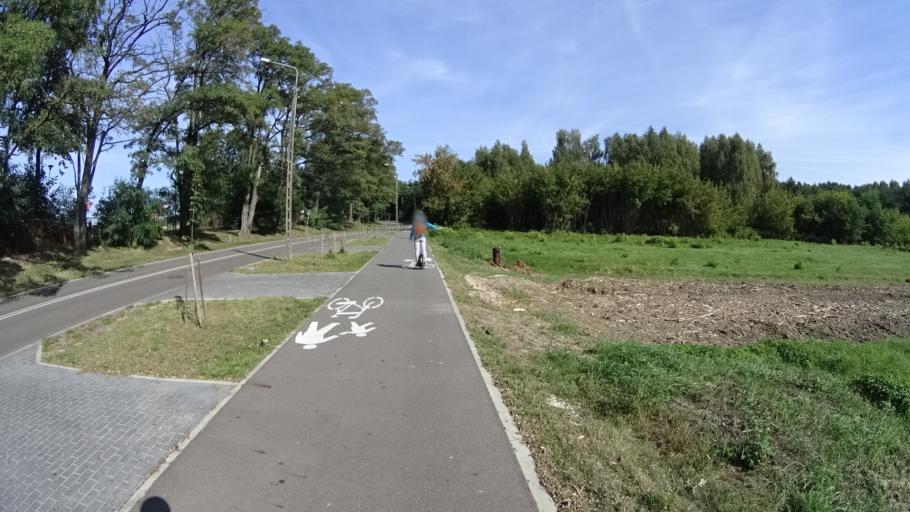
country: PL
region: Masovian Voivodeship
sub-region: Powiat legionowski
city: Bialobrzegi
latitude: 52.4504
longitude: 21.0654
